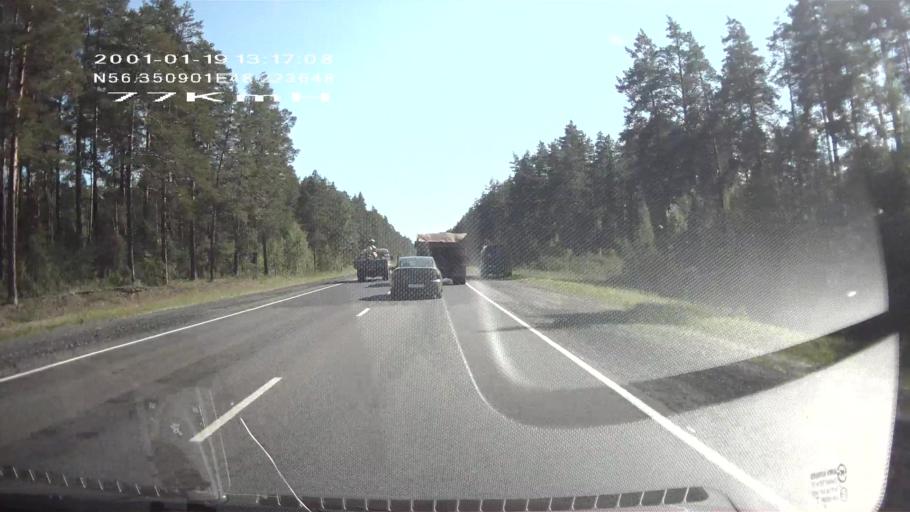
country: RU
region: Mariy-El
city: Suslonger
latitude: 56.3507
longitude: 48.2238
